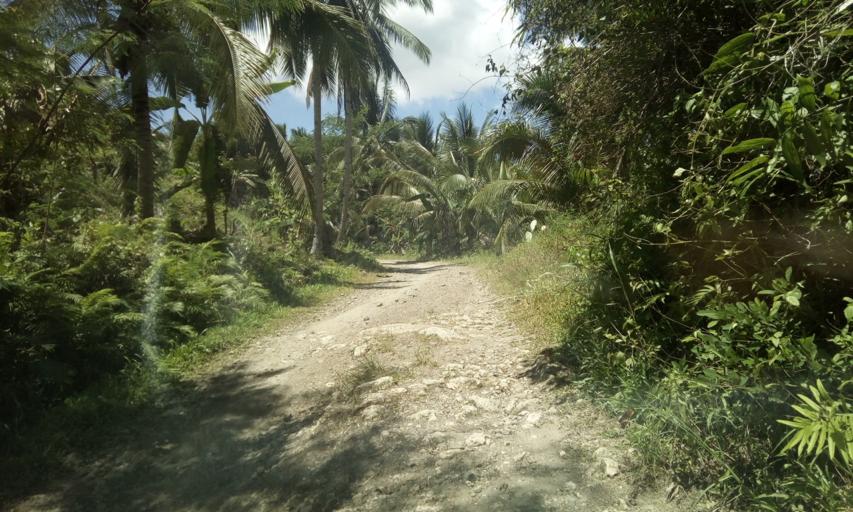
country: PH
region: Caraga
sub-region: Province of Agusan del Sur
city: Santa Josefa
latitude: 7.9552
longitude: 125.9923
